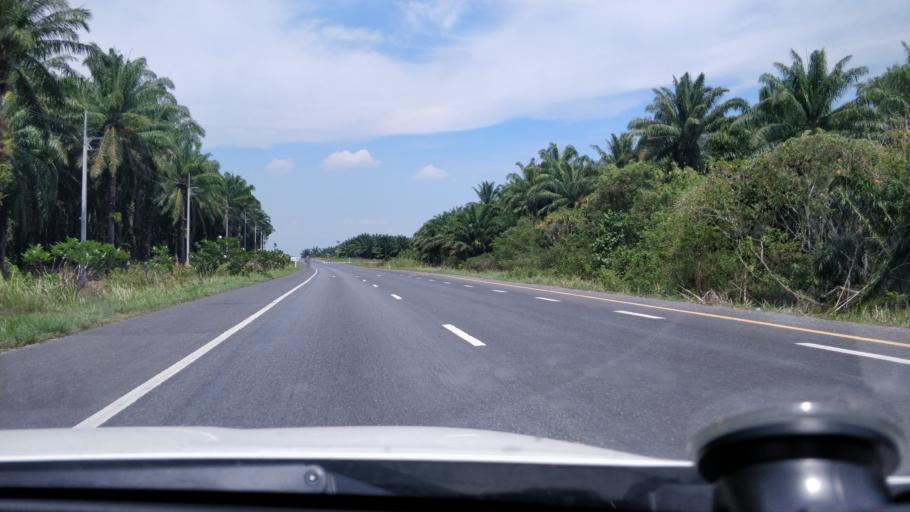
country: TH
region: Surat Thani
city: Chai Buri
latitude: 8.6413
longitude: 99.0821
